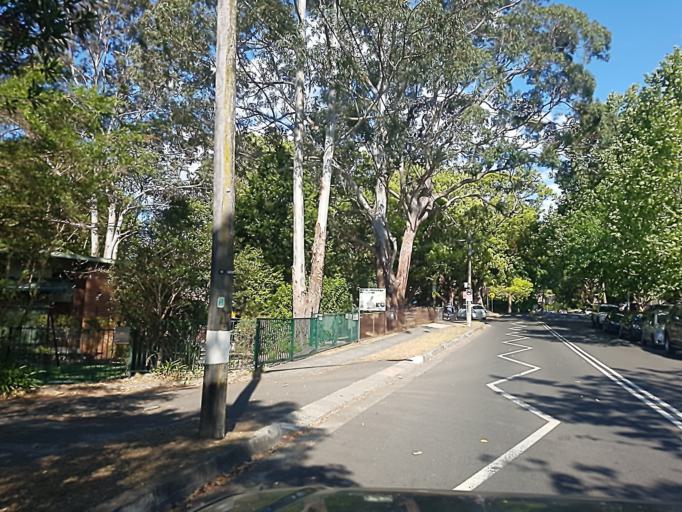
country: AU
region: New South Wales
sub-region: Ku-ring-gai
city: North Wahroonga
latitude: -33.7160
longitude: 151.1159
